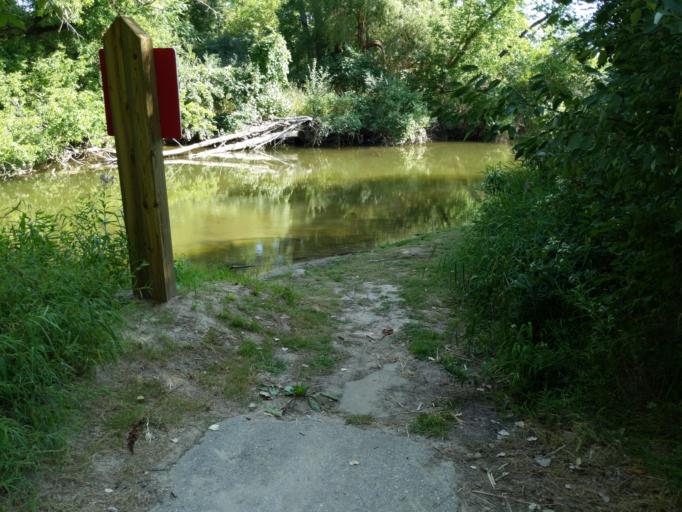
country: US
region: Michigan
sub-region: Isabella County
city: Mount Pleasant
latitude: 43.6013
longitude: -84.7841
